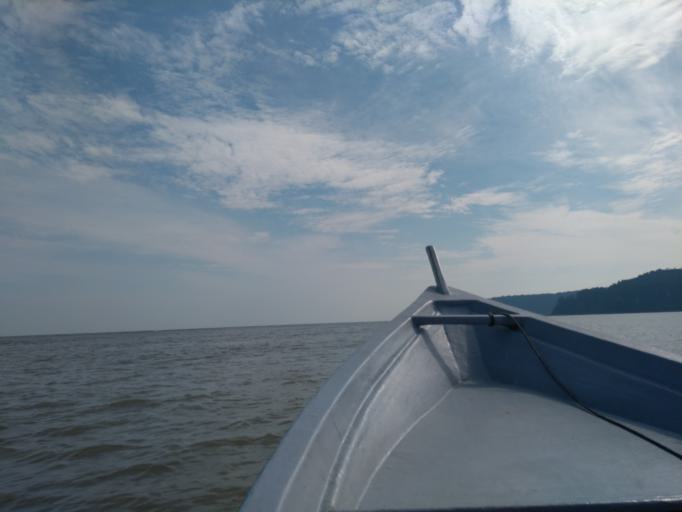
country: MY
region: Sarawak
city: Kuching
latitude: 1.7060
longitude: 110.4309
